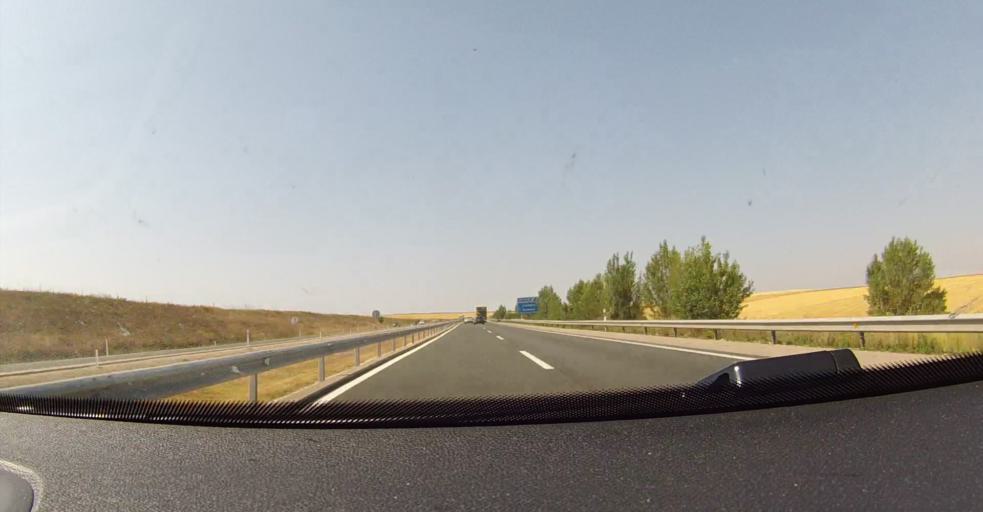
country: ES
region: Castille and Leon
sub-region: Provincia de Burgos
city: Zuneda
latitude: 42.5976
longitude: -3.2263
